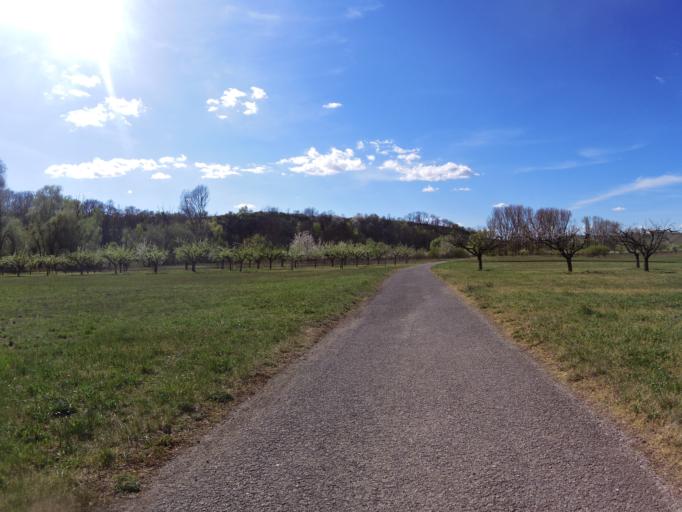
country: DE
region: Bavaria
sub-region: Regierungsbezirk Unterfranken
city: Volkach
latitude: 49.8551
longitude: 10.2089
